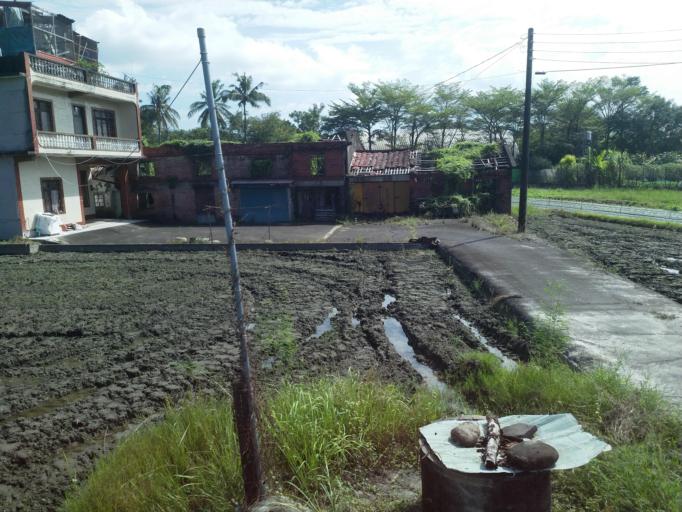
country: TW
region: Taiwan
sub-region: Pingtung
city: Pingtung
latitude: 22.8981
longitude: 120.5178
